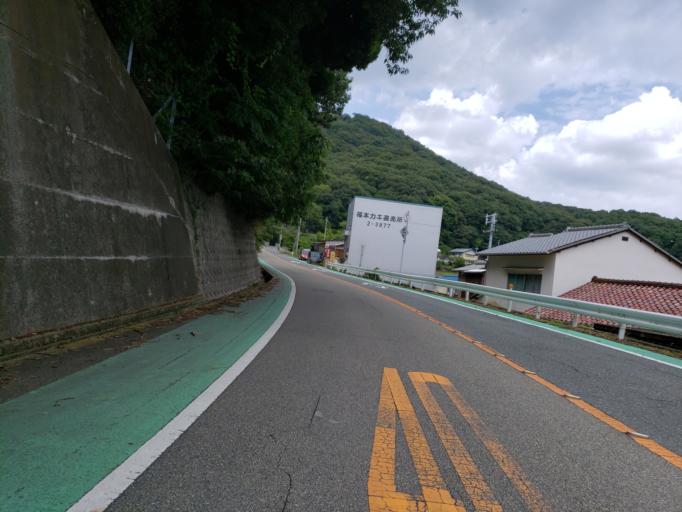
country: JP
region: Hyogo
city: Aioi
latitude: 34.7682
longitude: 134.4708
